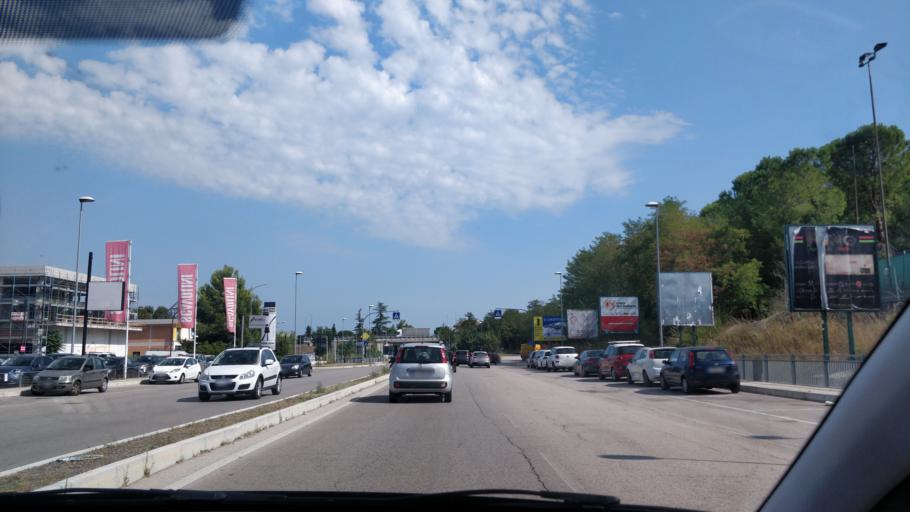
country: IT
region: Abruzzo
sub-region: Provincia di Chieti
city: Chieti
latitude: 42.3964
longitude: 14.1638
